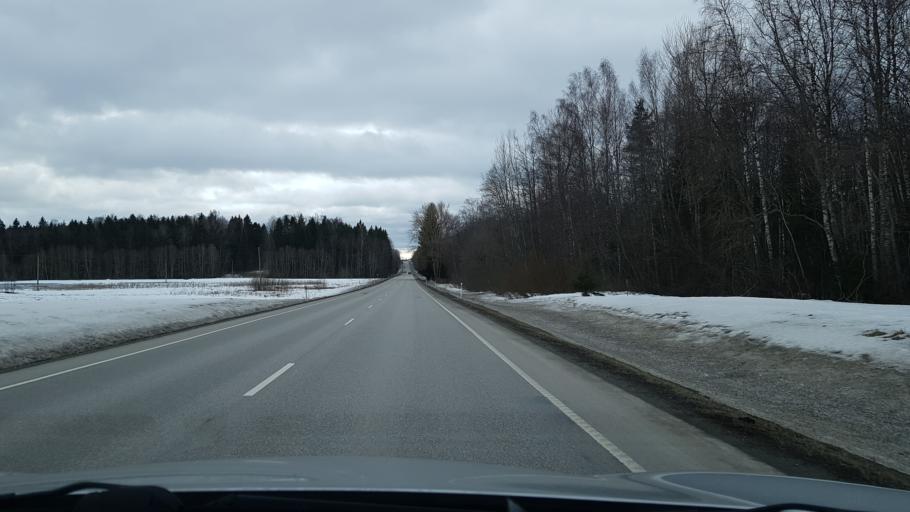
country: EE
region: Jogevamaa
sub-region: Tabivere vald
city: Tabivere
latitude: 58.5846
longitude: 26.5887
